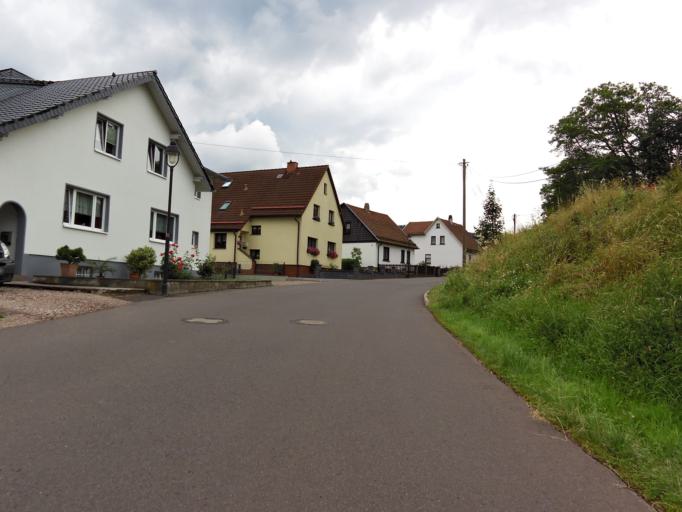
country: DE
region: Thuringia
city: Tabarz
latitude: 50.8871
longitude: 10.4824
